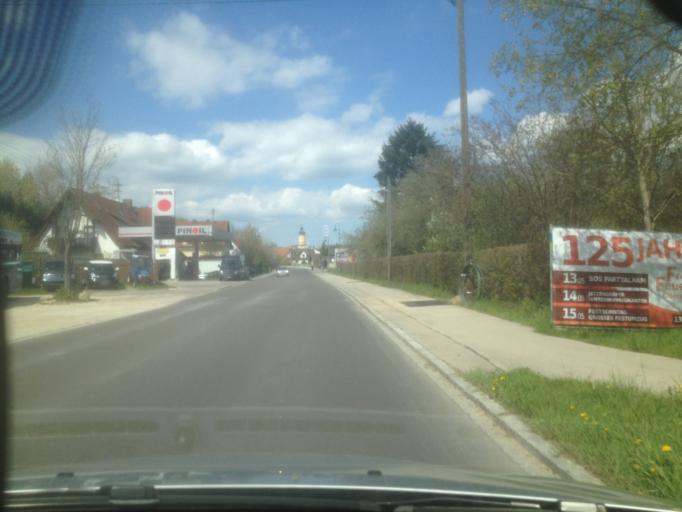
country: DE
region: Bavaria
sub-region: Swabia
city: Diedorf
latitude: 48.3734
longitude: 10.7683
